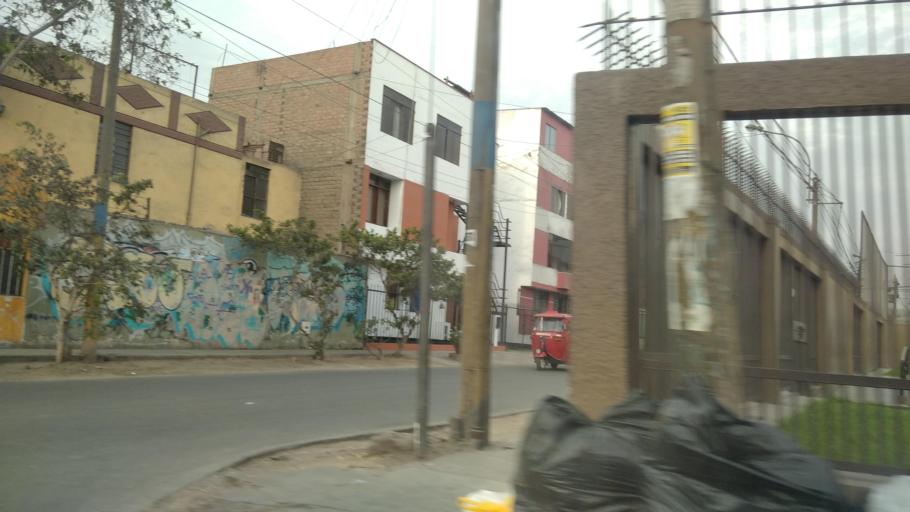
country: PE
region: Lima
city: Lima
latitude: -12.0237
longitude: -76.9968
